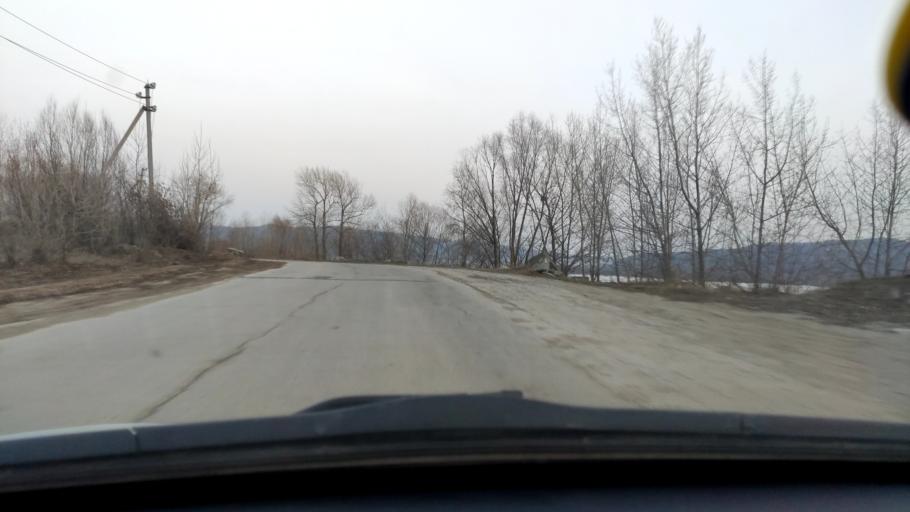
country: RU
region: Samara
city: Zhigulevsk
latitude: 53.4582
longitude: 49.5126
